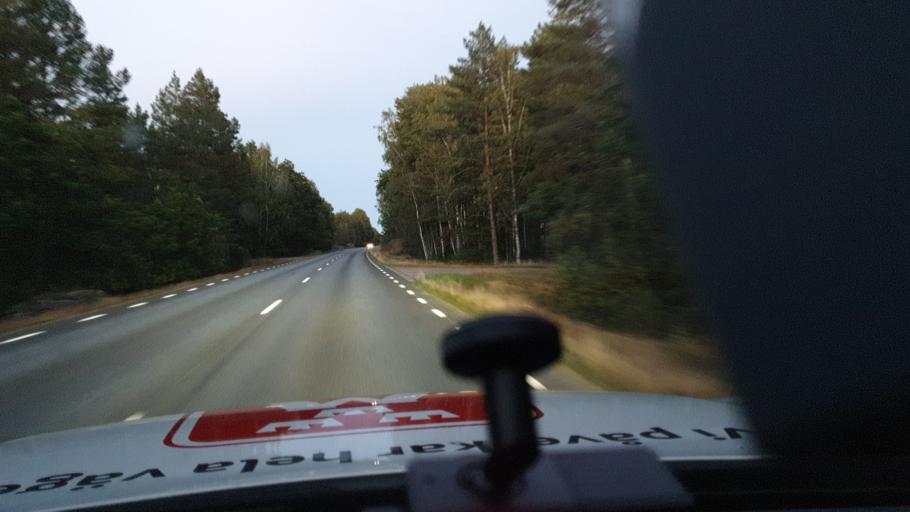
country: SE
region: Kalmar
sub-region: Oskarshamns Kommun
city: Paskallavik
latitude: 57.1844
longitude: 16.3954
